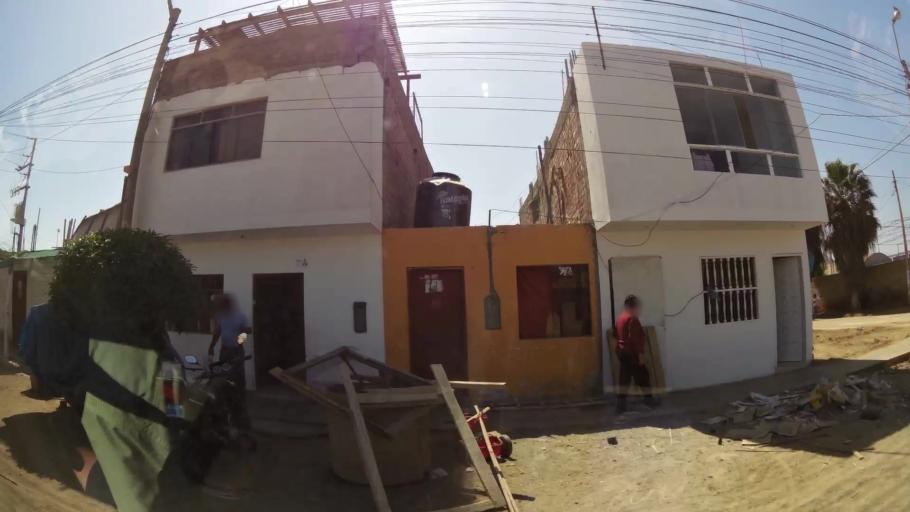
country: PE
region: Lima
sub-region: Provincia de Canete
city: San Vicente de Canete
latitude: -13.0223
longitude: -76.4791
